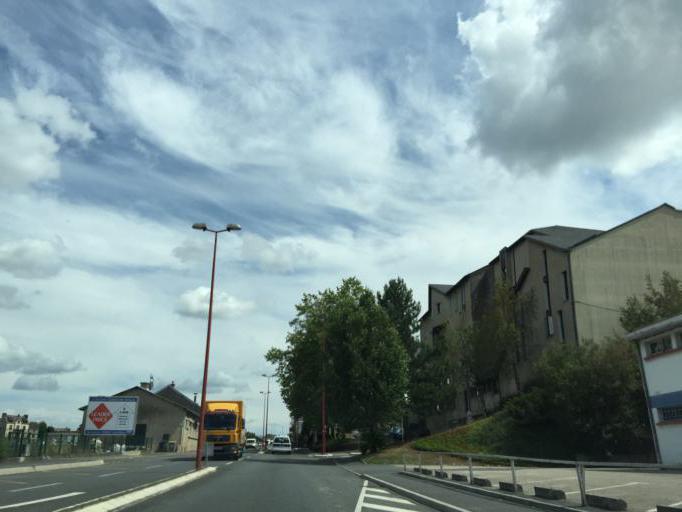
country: FR
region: Midi-Pyrenees
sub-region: Departement de l'Aveyron
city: Rodez
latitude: 44.3619
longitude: 2.5828
